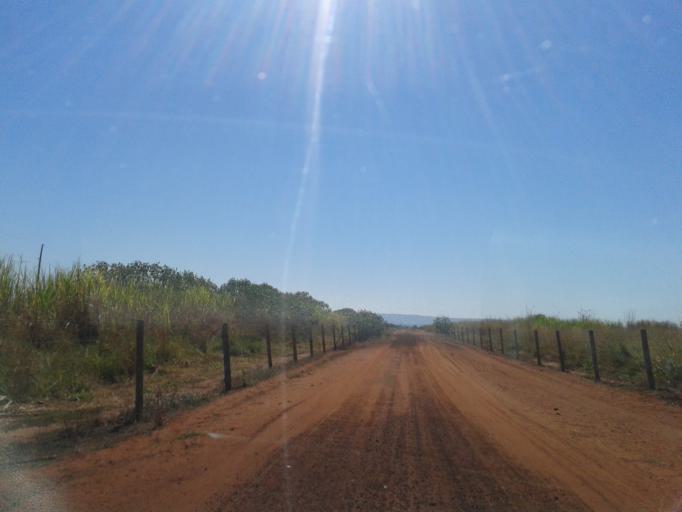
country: BR
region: Minas Gerais
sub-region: Santa Vitoria
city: Santa Vitoria
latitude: -19.1464
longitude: -50.2032
